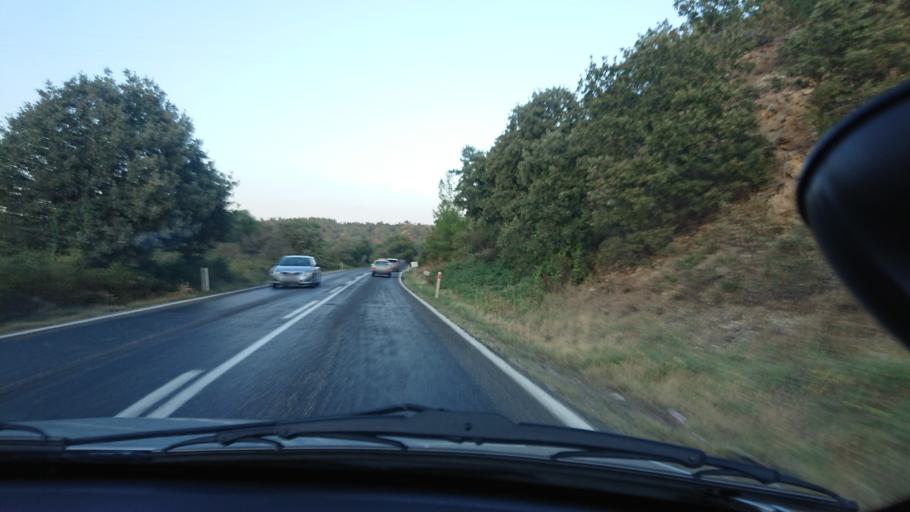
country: TR
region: Usak
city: Gure
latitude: 38.8131
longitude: 29.2473
